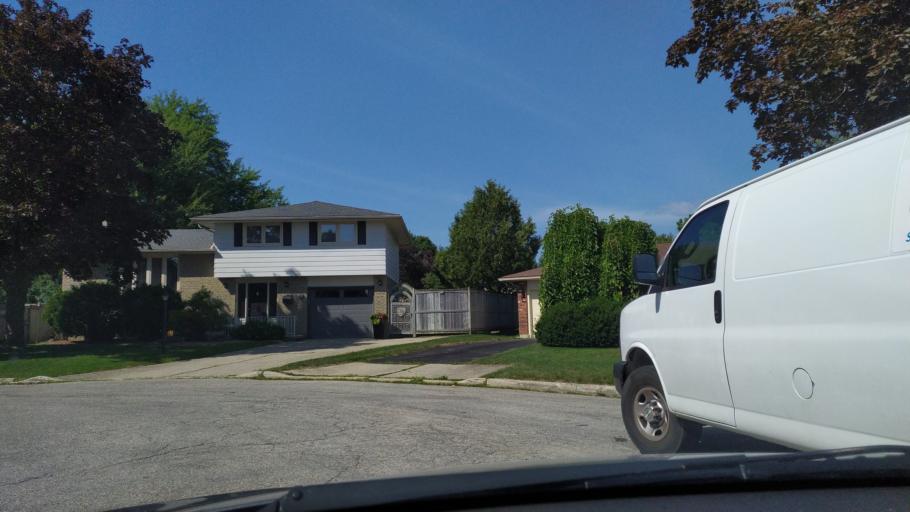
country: CA
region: Ontario
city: Stratford
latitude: 43.3852
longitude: -80.9663
